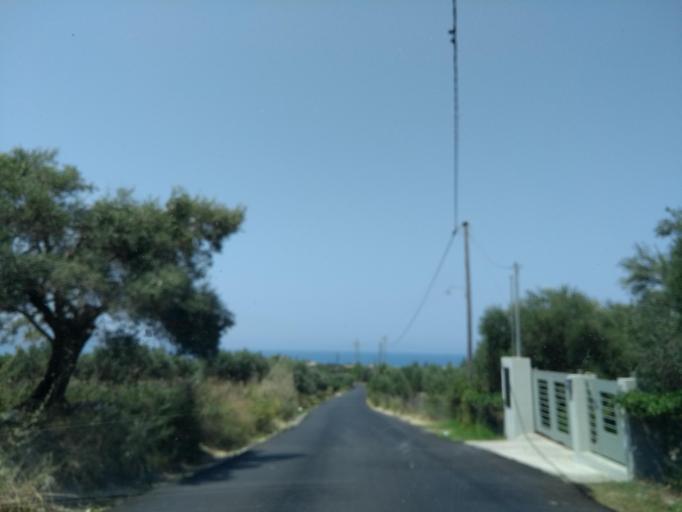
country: GR
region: Crete
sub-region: Nomos Chanias
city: Georgioupolis
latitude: 35.3352
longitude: 24.3019
